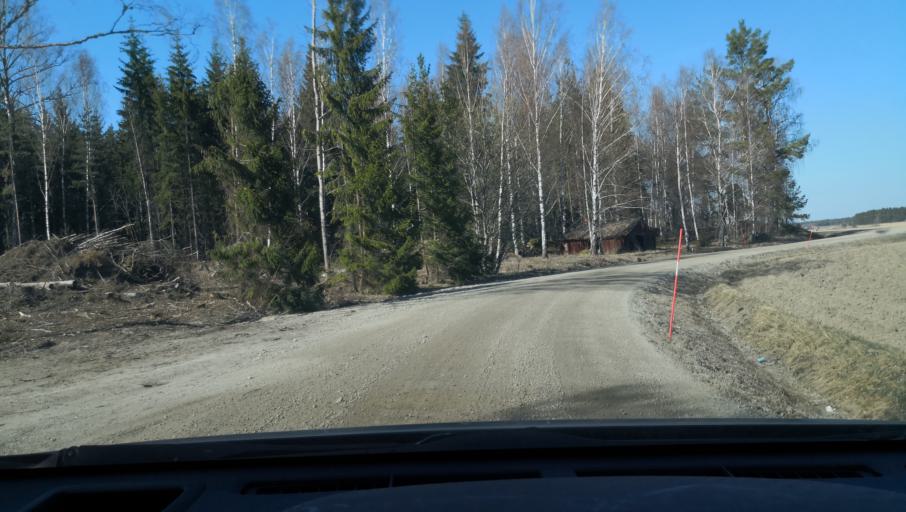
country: SE
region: Vaestmanland
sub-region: Sala Kommun
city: Sala
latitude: 59.8849
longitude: 16.5274
